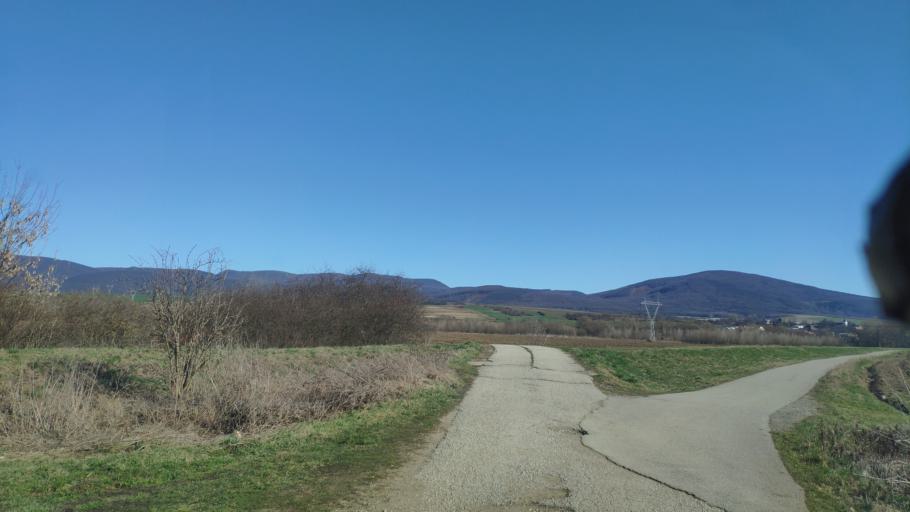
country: HU
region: Borsod-Abauj-Zemplen
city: Gonc
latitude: 48.5868
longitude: 21.3225
